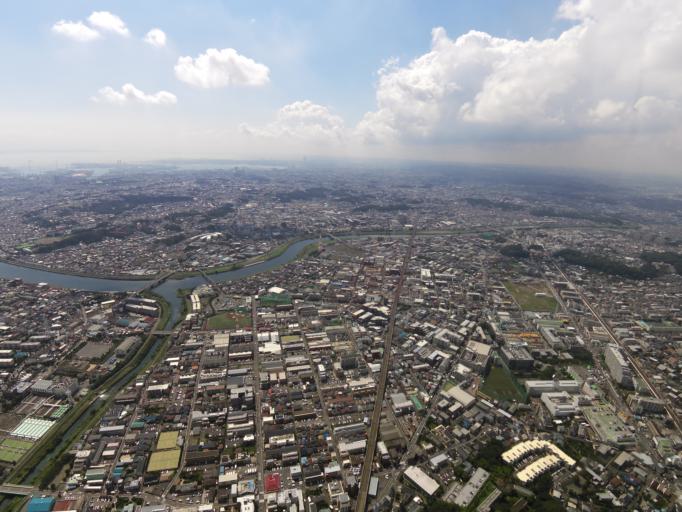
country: JP
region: Kanagawa
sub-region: Kawasaki-shi
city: Kawasaki
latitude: 35.5495
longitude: 139.6518
